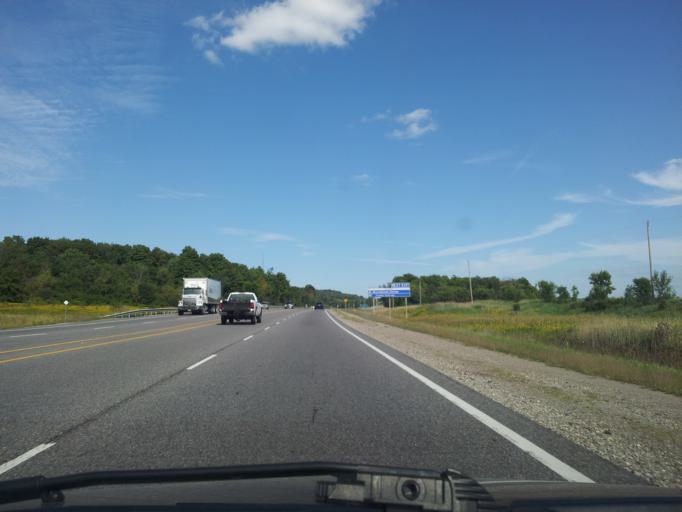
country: CA
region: Ontario
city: Kitchener
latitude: 43.3900
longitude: -80.6718
